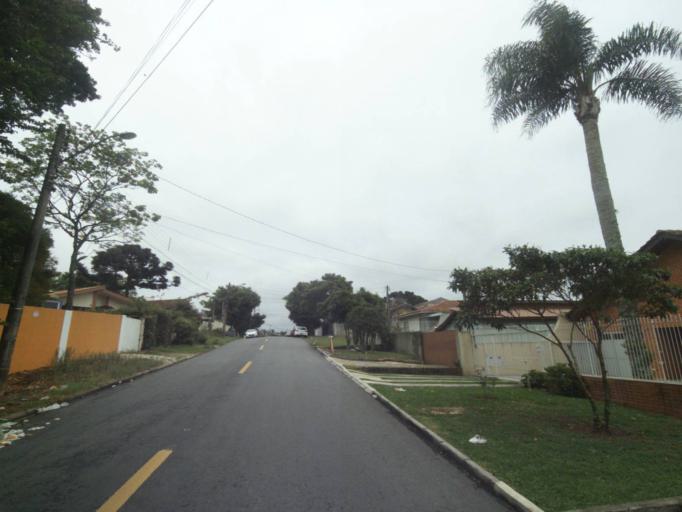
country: BR
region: Parana
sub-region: Curitiba
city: Curitiba
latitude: -25.4097
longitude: -49.2904
